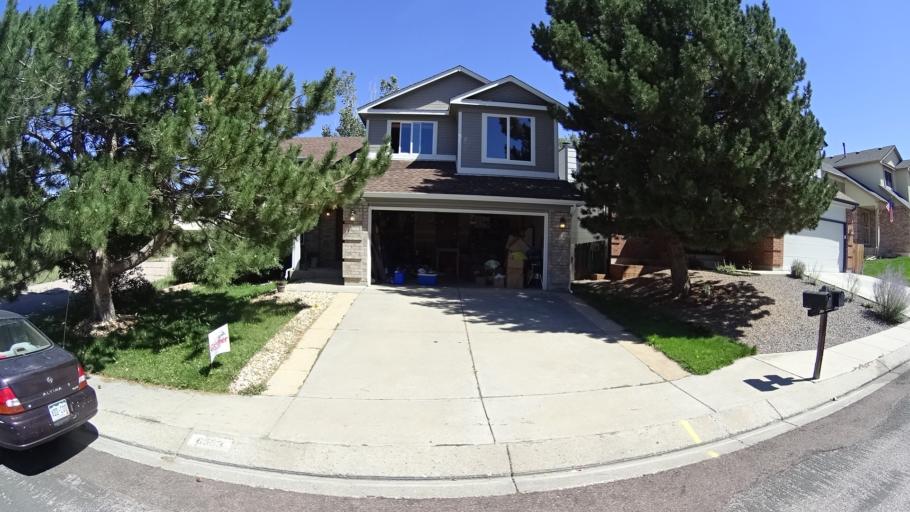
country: US
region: Colorado
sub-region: El Paso County
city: Colorado Springs
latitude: 38.9274
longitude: -104.7819
